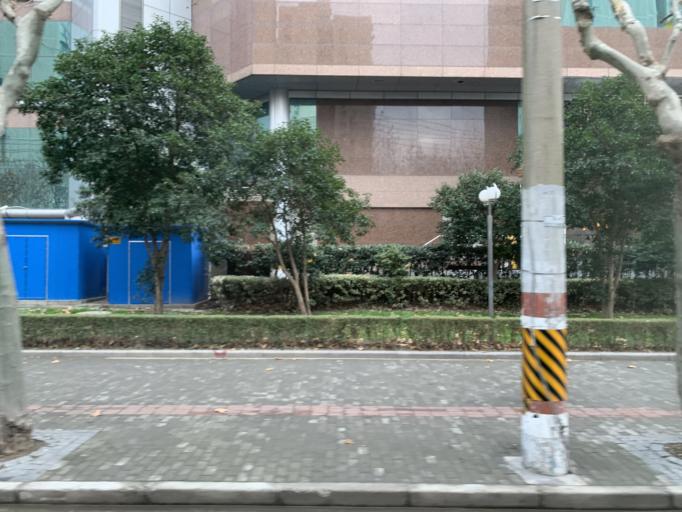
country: CN
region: Shanghai Shi
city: Pudong
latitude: 31.2283
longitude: 121.5193
